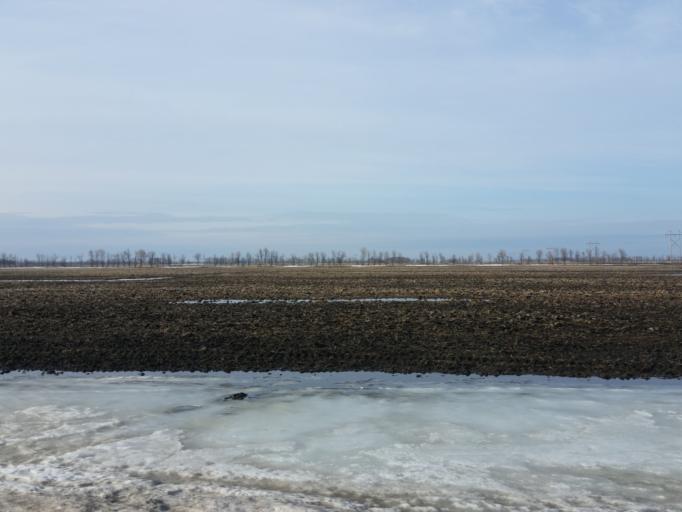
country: US
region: North Dakota
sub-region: Walsh County
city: Grafton
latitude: 48.4267
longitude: -97.2684
